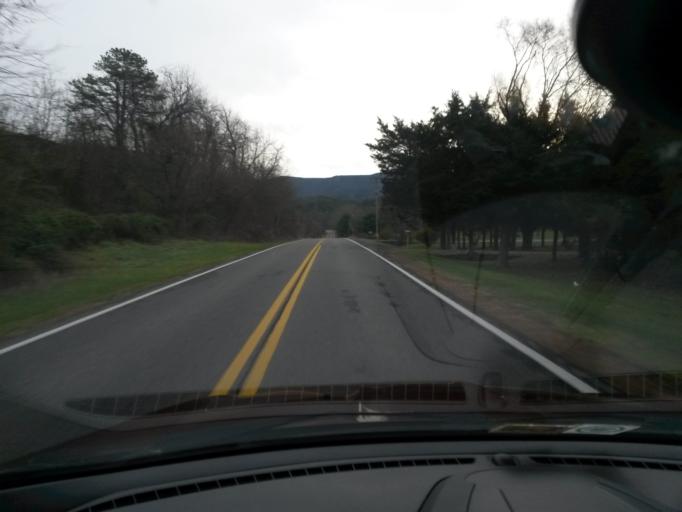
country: US
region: Virginia
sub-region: Alleghany County
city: Clifton Forge
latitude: 37.7950
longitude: -79.7239
